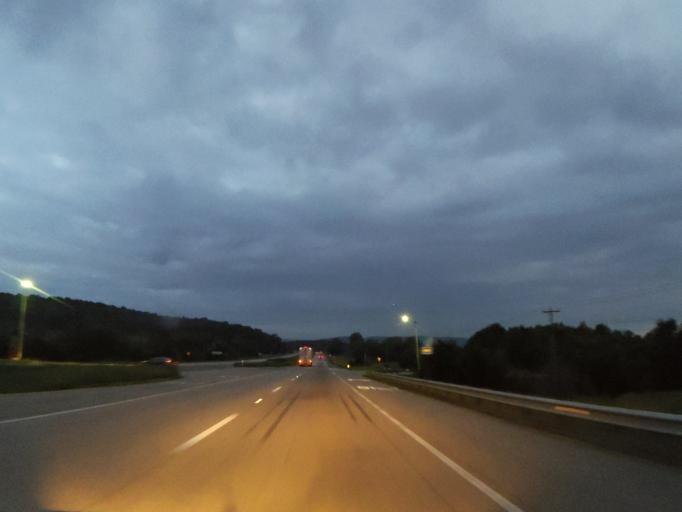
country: US
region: Alabama
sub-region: Madison County
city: New Hope
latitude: 34.6090
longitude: -86.2715
